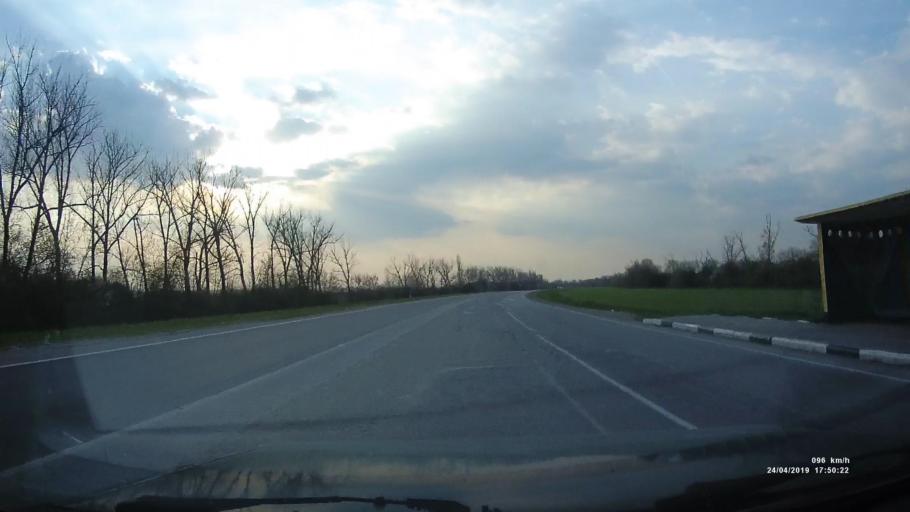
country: RU
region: Rostov
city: Yegorlykskaya
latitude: 46.5402
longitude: 40.7818
